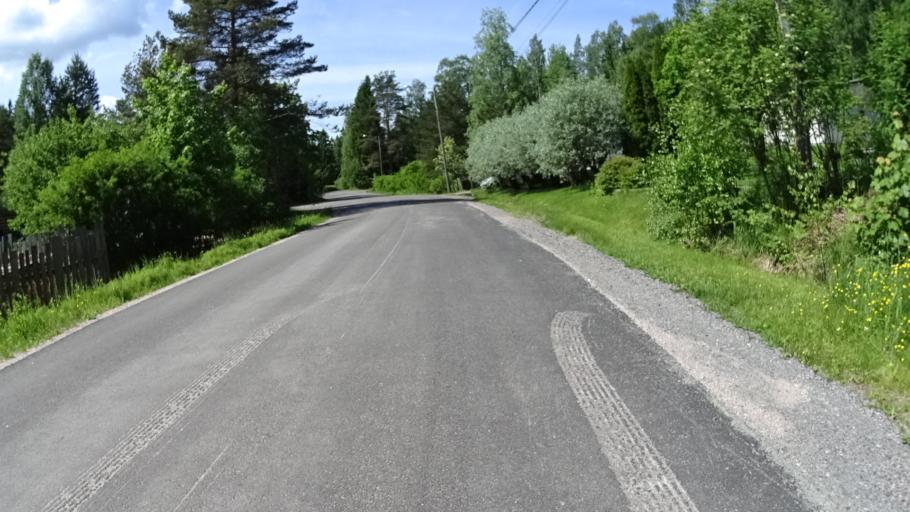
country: FI
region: Uusimaa
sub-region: Helsinki
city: Kauniainen
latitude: 60.3210
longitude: 24.7326
